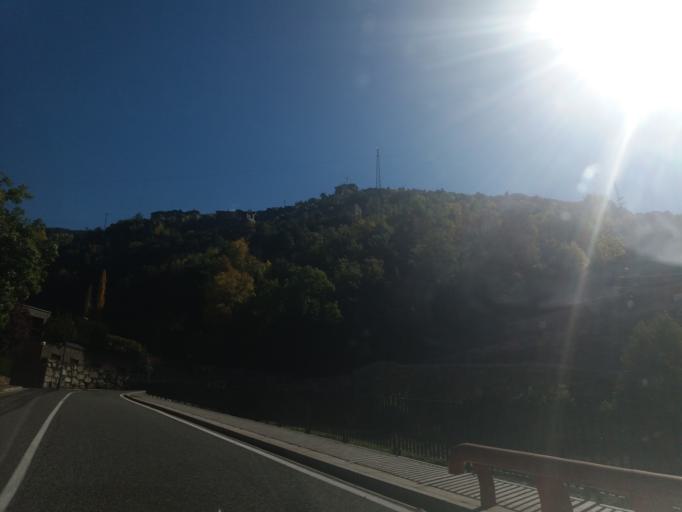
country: AD
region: Sant Julia de Loria
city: Sant Julia de Loria
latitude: 42.4647
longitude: 1.4940
